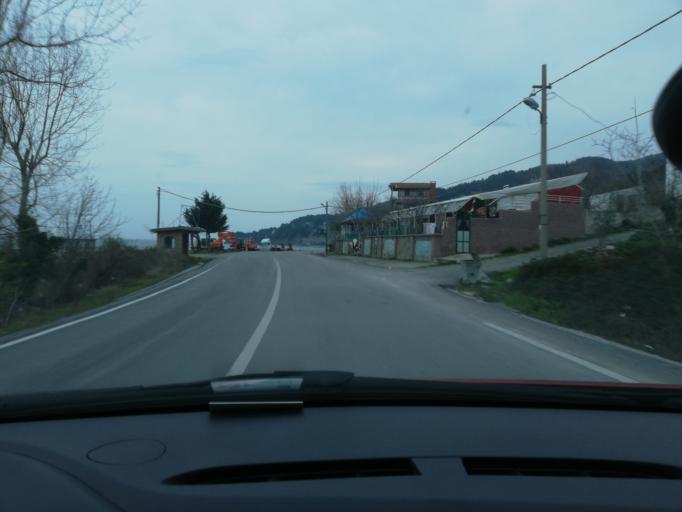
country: TR
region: Kastamonu
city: Inebolu
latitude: 41.9728
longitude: 33.7927
